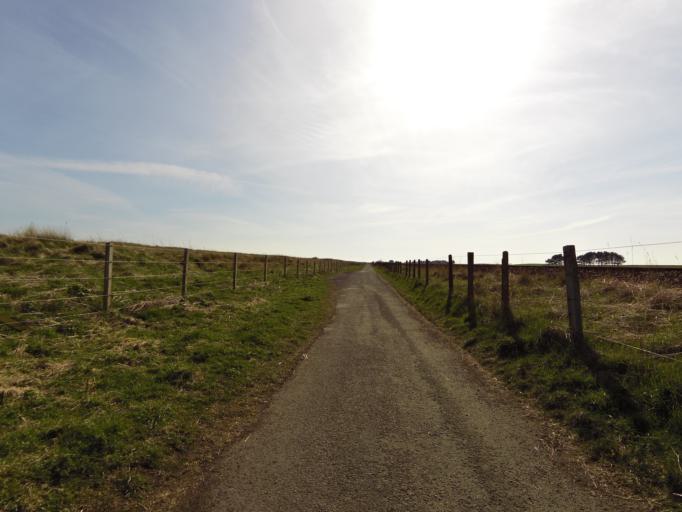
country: GB
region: Scotland
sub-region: Angus
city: Arbroath
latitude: 56.5387
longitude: -2.6260
